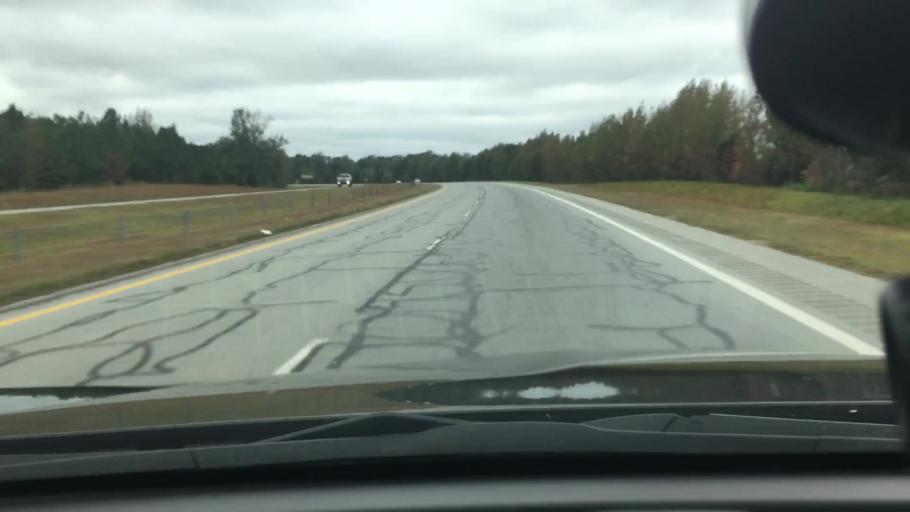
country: US
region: North Carolina
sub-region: Pitt County
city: Farmville
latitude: 35.6179
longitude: -77.5878
